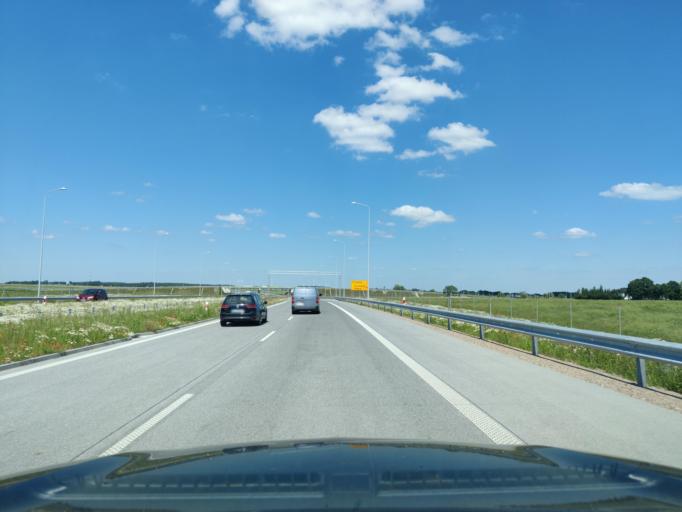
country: PL
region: Masovian Voivodeship
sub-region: Powiat mlawski
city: Wisniewo
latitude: 52.9857
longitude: 20.3434
